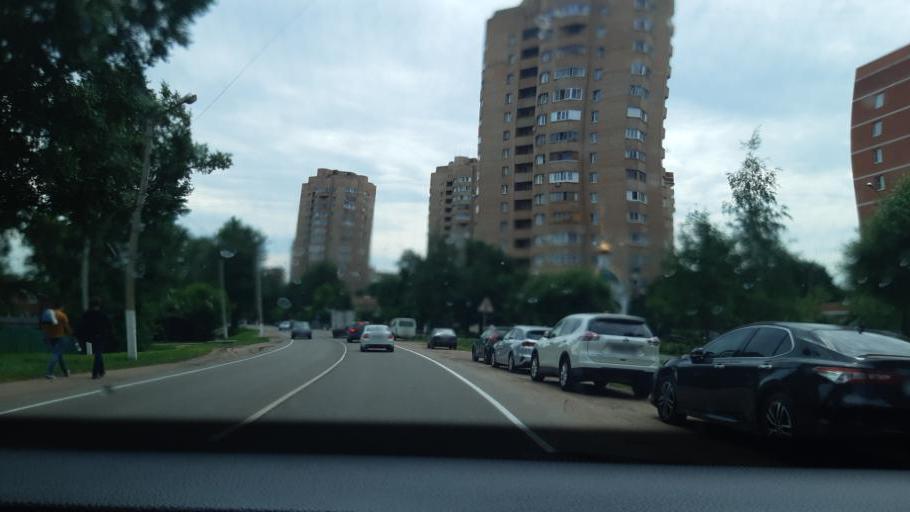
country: RU
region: Moskovskaya
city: Bol'shiye Vyazemy
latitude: 55.6255
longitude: 36.9832
